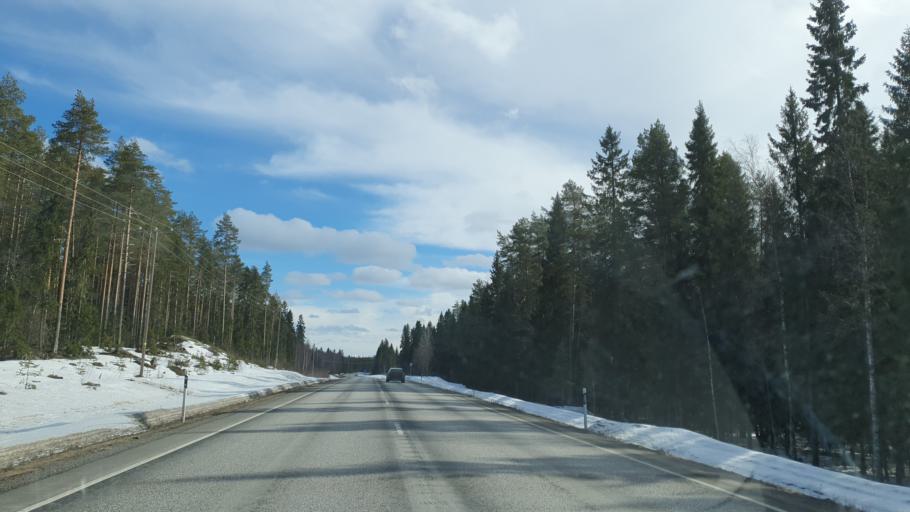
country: FI
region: Kainuu
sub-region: Kajaani
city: Paltamo
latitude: 64.3850
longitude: 28.0050
